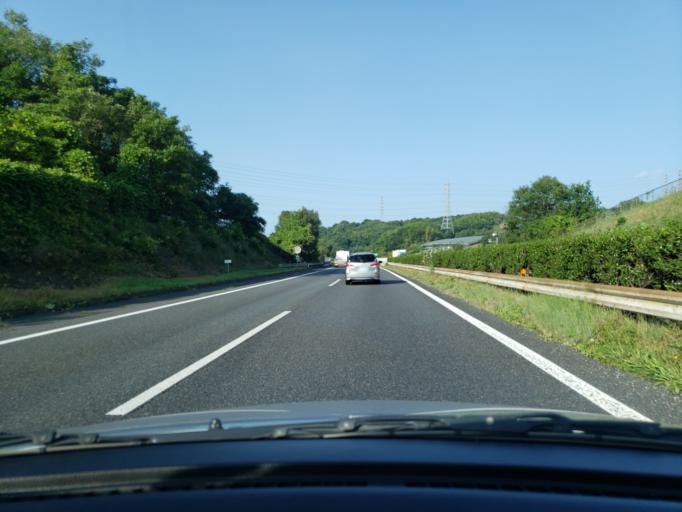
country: JP
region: Okayama
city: Kurashiki
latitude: 34.5987
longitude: 133.7006
